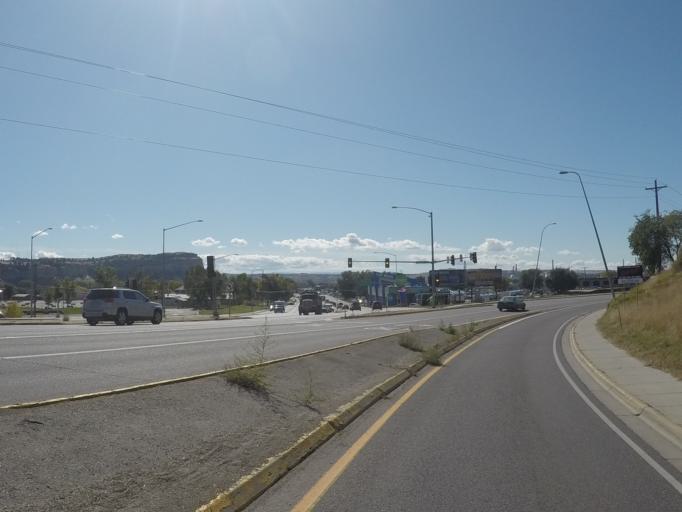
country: US
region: Montana
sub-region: Yellowstone County
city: Billings
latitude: 45.7999
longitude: -108.4814
